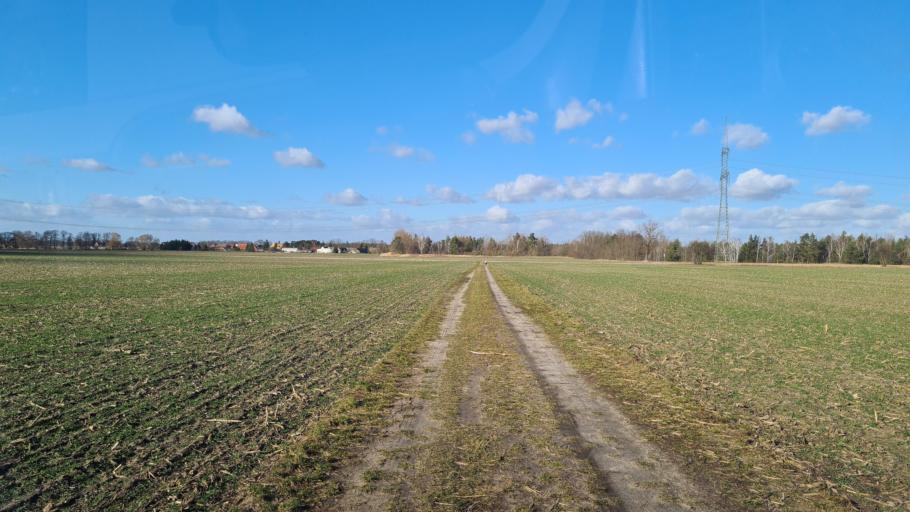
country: DE
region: Brandenburg
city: Finsterwalde
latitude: 51.6559
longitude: 13.6877
